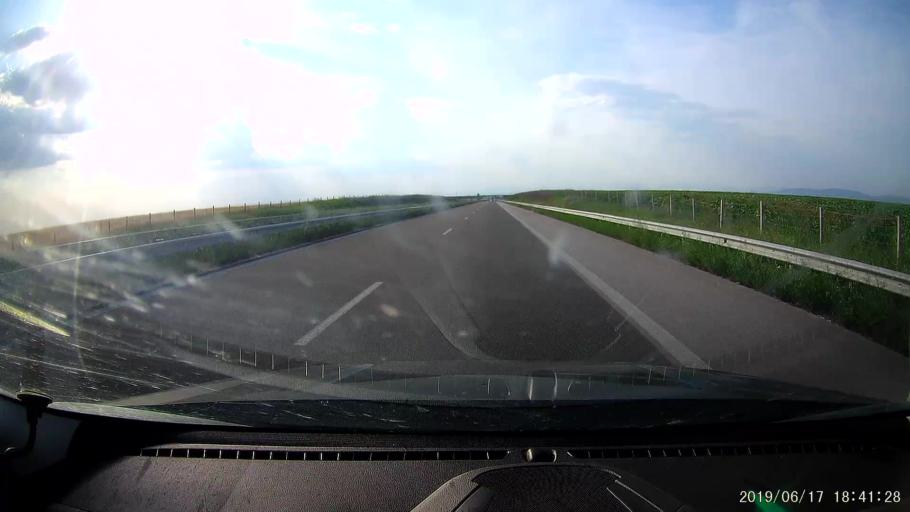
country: BG
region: Stara Zagora
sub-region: Obshtina Chirpan
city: Chirpan
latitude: 42.1729
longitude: 25.2552
